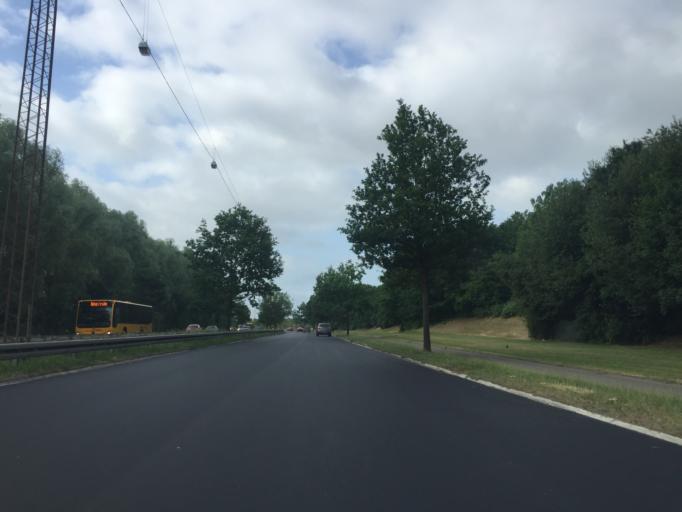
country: DK
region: Capital Region
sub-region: Rodovre Kommune
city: Rodovre
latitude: 55.6614
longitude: 12.4545
